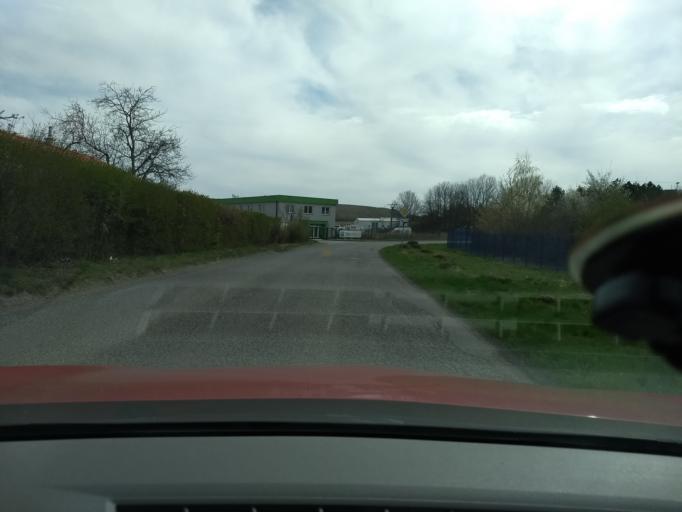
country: CZ
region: Central Bohemia
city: Hostivice
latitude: 50.0643
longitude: 14.2374
